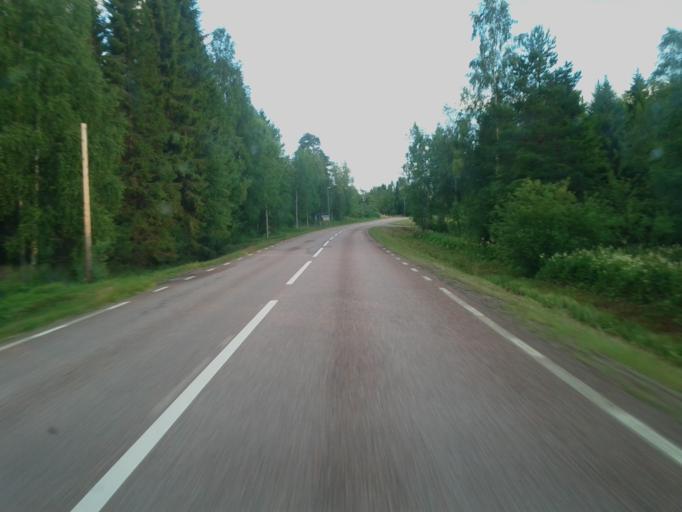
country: SE
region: Dalarna
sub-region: Borlange Kommun
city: Borlaenge
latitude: 60.3439
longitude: 15.4043
